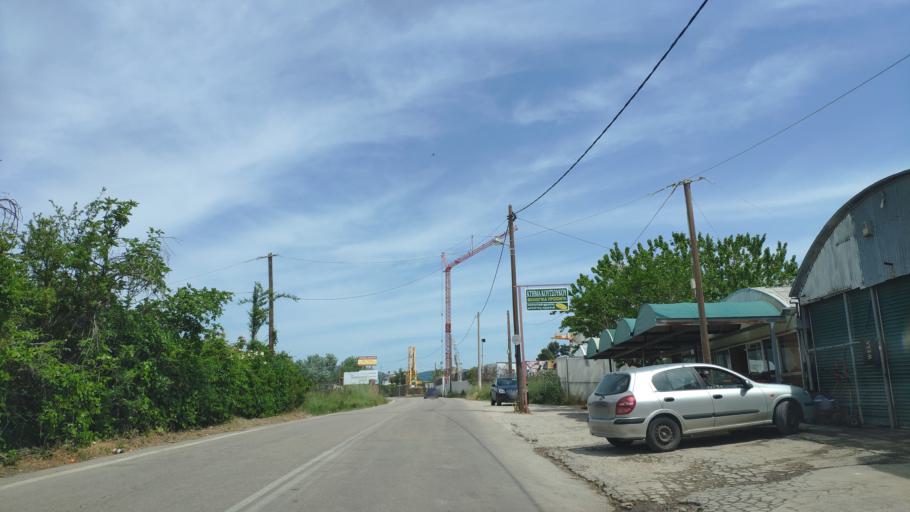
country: GR
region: Attica
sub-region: Nomarchia Anatolikis Attikis
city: Afidnes
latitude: 38.1819
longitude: 23.8565
